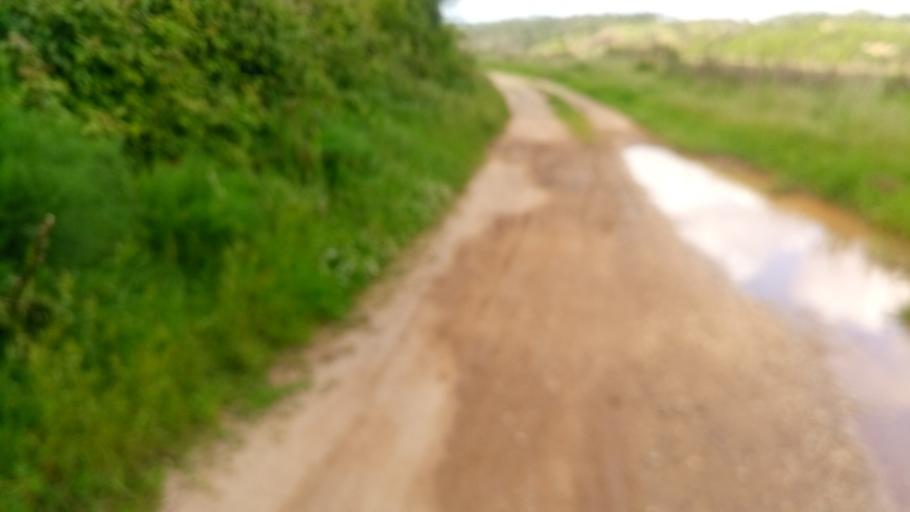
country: PT
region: Leiria
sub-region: Obidos
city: Obidos
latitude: 39.3899
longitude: -9.1987
